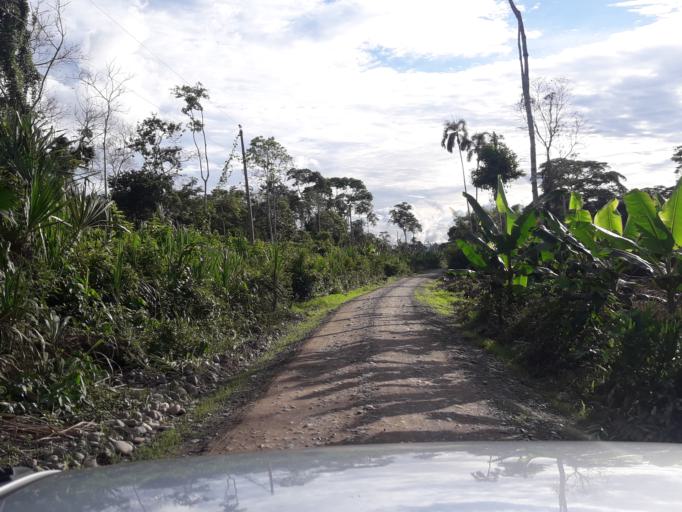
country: EC
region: Orellana
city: Boca Suno
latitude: -0.8829
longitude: -77.2879
